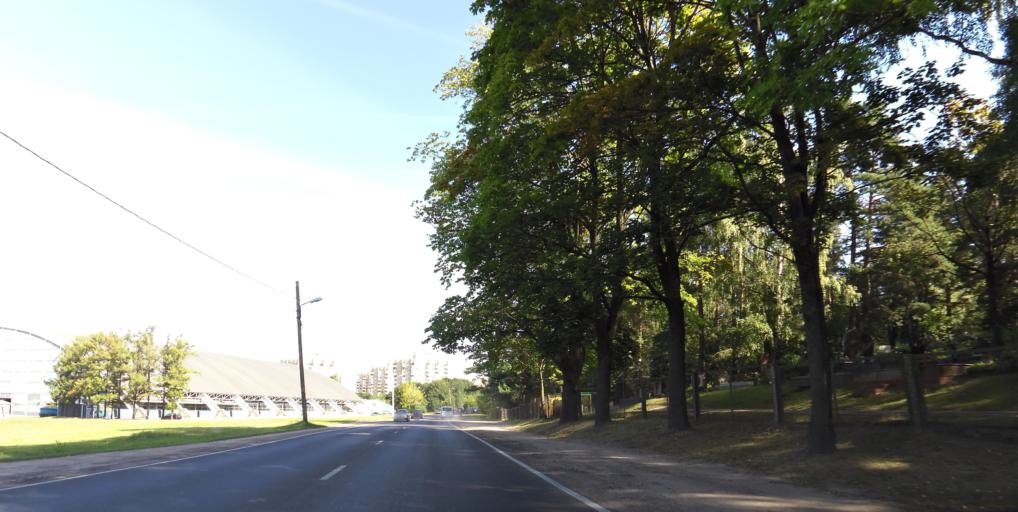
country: LT
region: Vilnius County
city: Seskine
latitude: 54.7062
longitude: 25.2378
